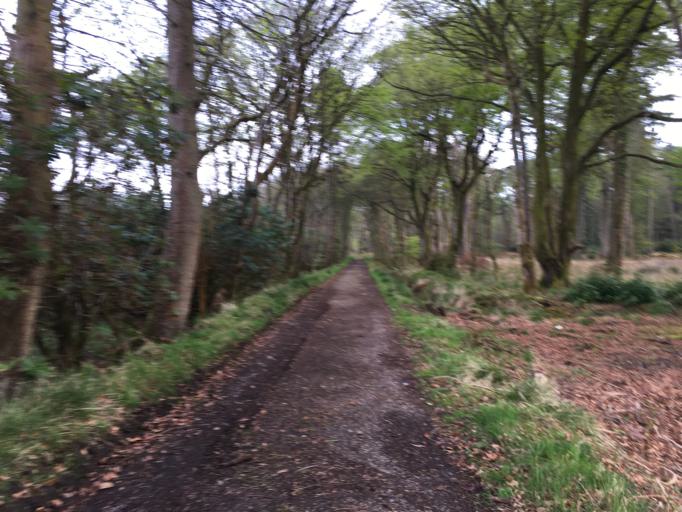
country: GB
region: Scotland
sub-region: Argyll and Bute
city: Rothesay
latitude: 55.8008
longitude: -5.0164
